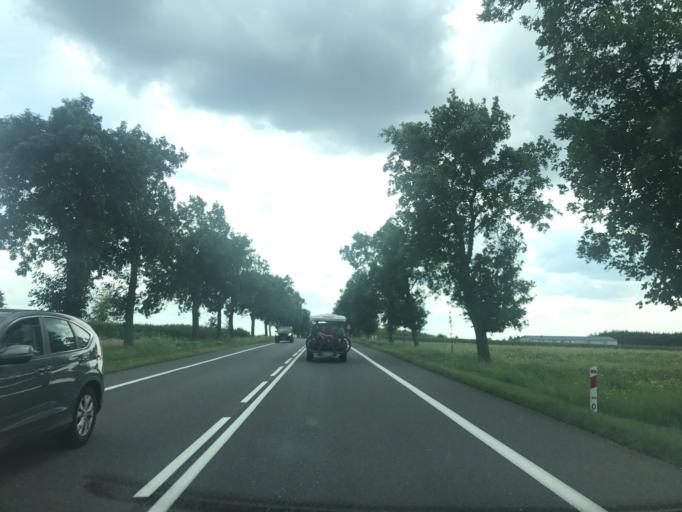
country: PL
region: Masovian Voivodeship
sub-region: Powiat mlawski
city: Wisniewo
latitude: 53.0275
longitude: 20.3368
